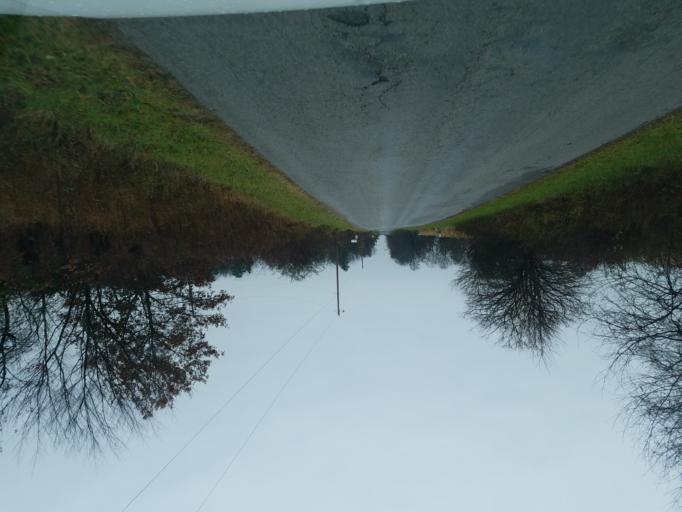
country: US
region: Ohio
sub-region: Knox County
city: Centerburg
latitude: 40.3630
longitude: -82.7034
